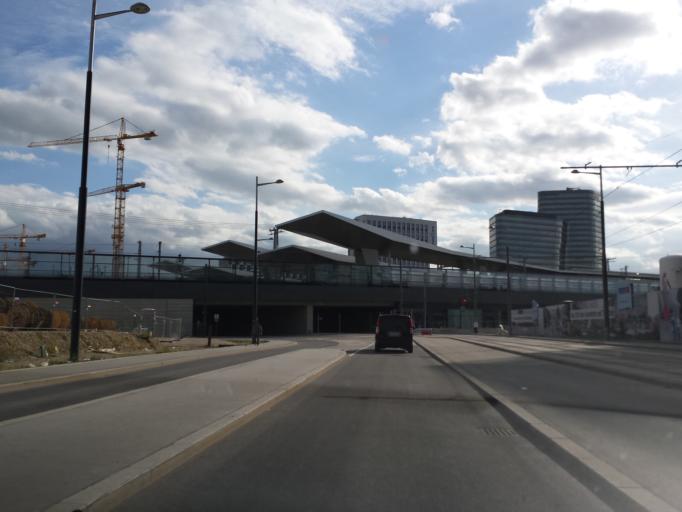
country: AT
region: Vienna
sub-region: Wien Stadt
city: Vienna
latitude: 48.1858
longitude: 16.3818
